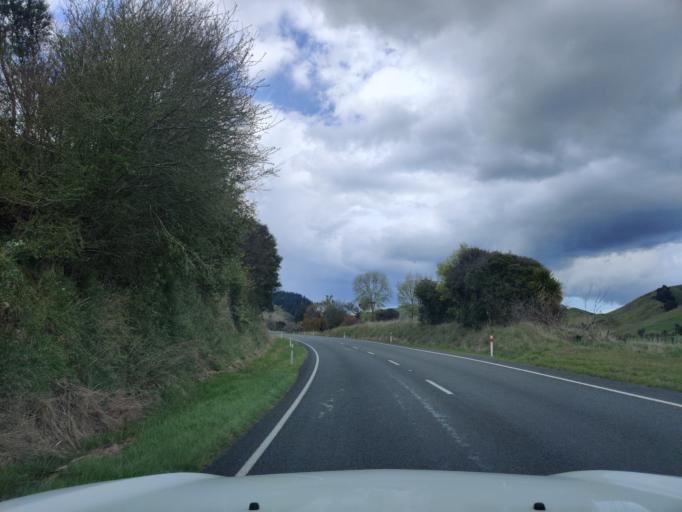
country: NZ
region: Manawatu-Wanganui
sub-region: Wanganui District
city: Wanganui
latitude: -39.8481
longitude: 175.1408
